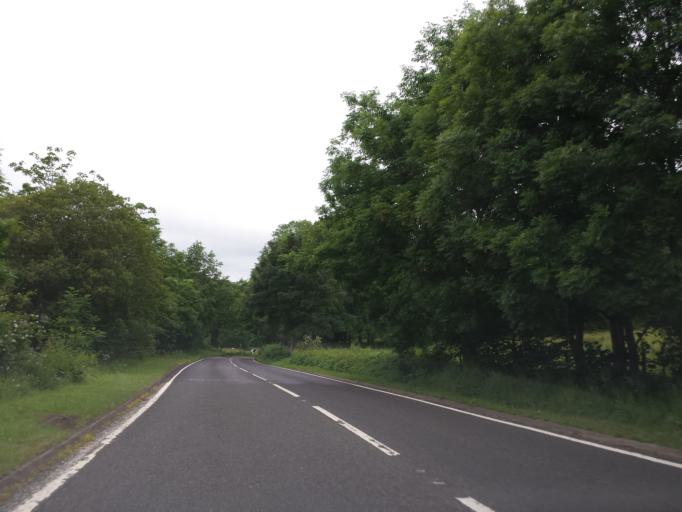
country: GB
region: Scotland
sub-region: Stirling
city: Callander
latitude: 56.3912
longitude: -4.2069
